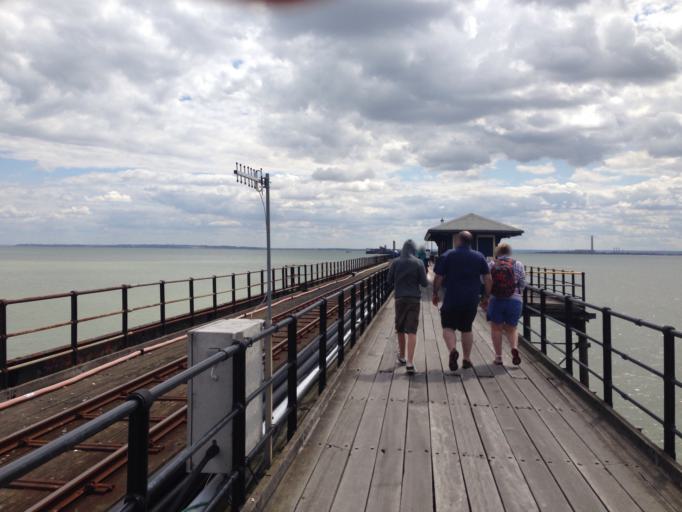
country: GB
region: England
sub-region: Southend-on-Sea
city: Southend-on-Sea
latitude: 51.5260
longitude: 0.7181
